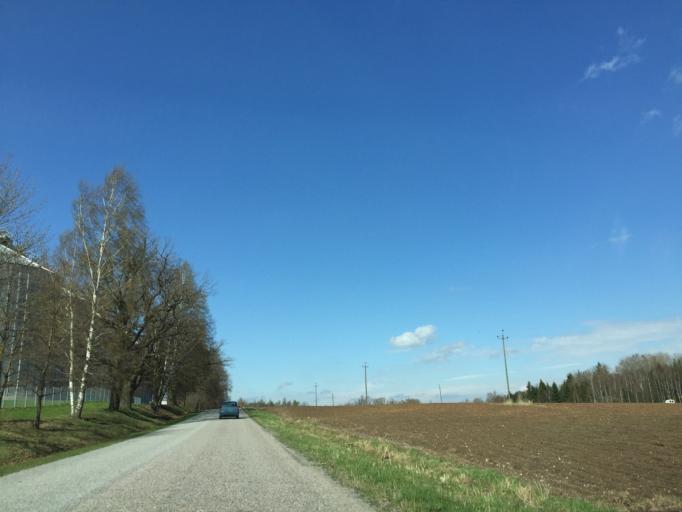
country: EE
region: Tartu
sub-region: Elva linn
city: Elva
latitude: 58.1473
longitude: 26.2337
